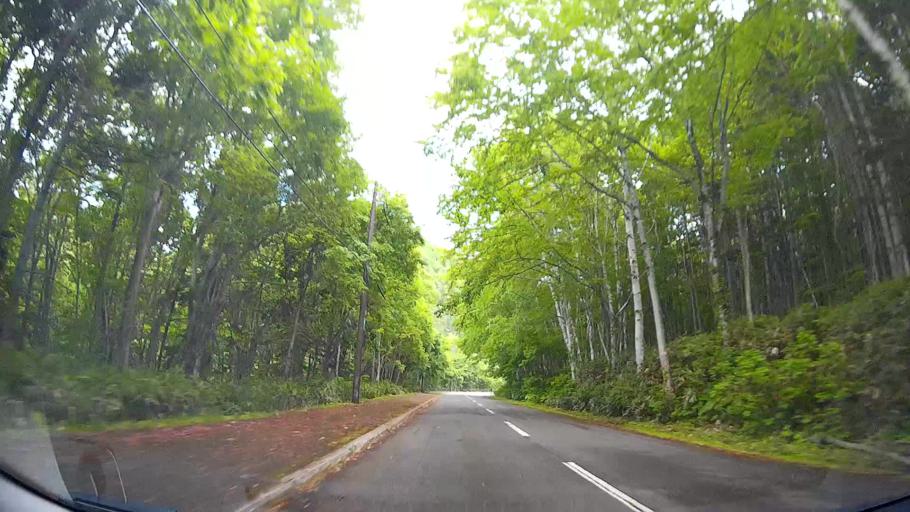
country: JP
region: Hokkaido
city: Sapporo
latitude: 42.9309
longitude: 141.1583
